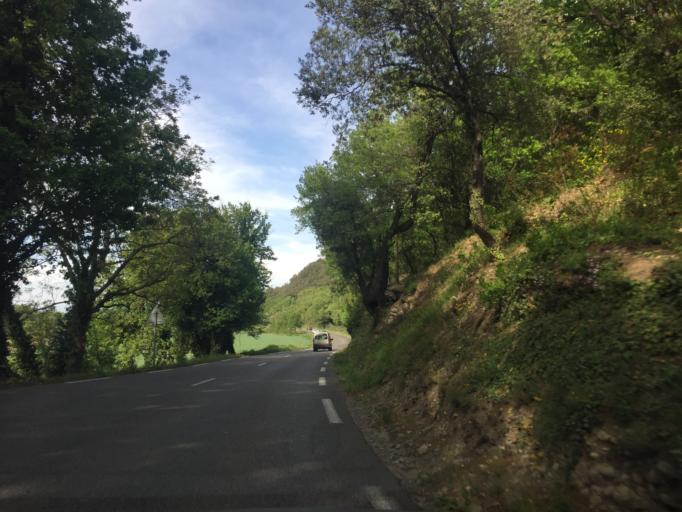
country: FR
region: Provence-Alpes-Cote d'Azur
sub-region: Departement des Alpes-de-Haute-Provence
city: Sainte-Tulle
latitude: 43.7787
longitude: 5.8185
